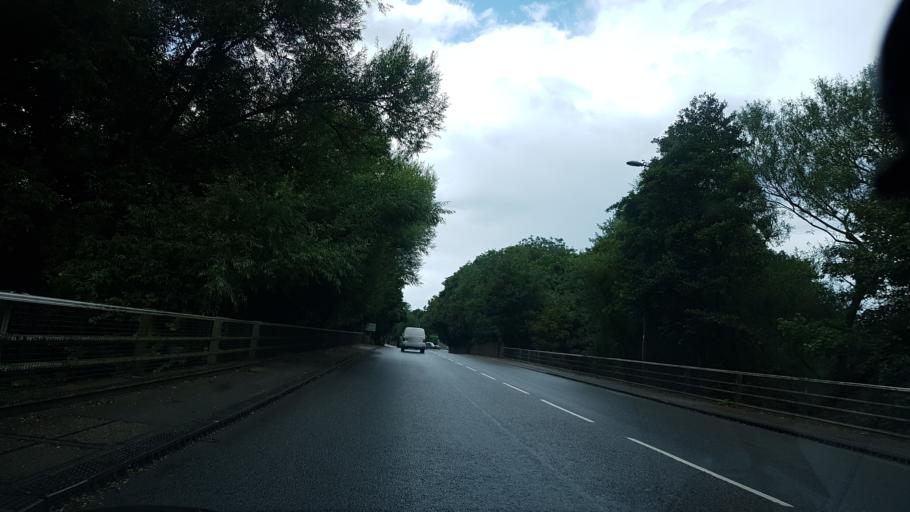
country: GB
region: England
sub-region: Surrey
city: Byfleet
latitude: 51.3410
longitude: -0.4641
